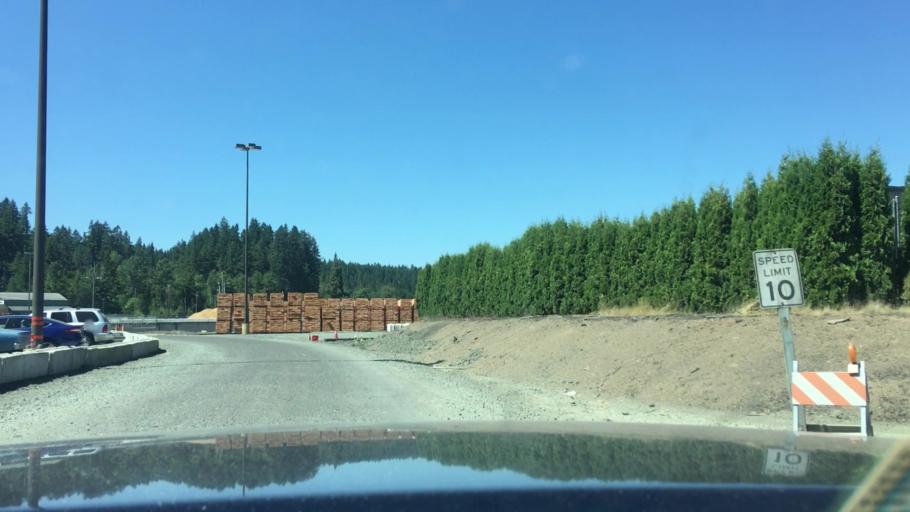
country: US
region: Oregon
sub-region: Lane County
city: Cottage Grove
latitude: 43.7672
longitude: -123.0776
